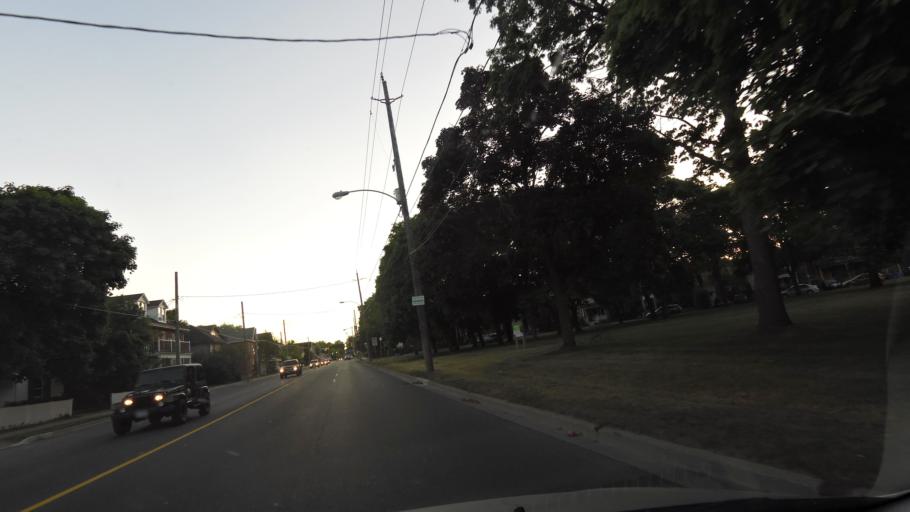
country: CA
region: Ontario
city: Peterborough
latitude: 44.3167
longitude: -78.3170
